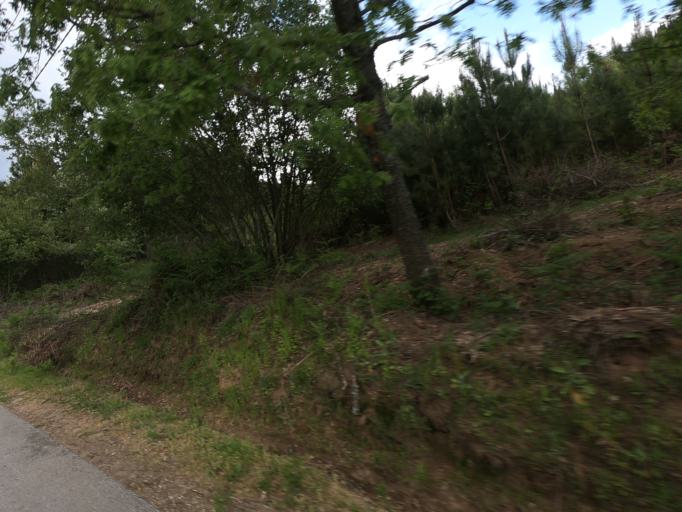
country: PT
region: Vila Real
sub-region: Vila Real
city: Vila Real
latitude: 41.2938
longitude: -7.7011
